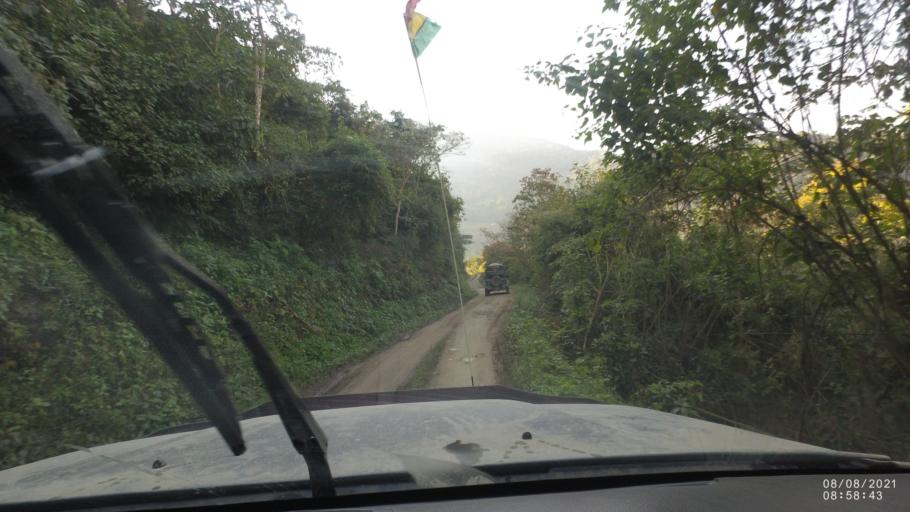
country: BO
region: La Paz
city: Quime
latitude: -16.5500
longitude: -66.7426
